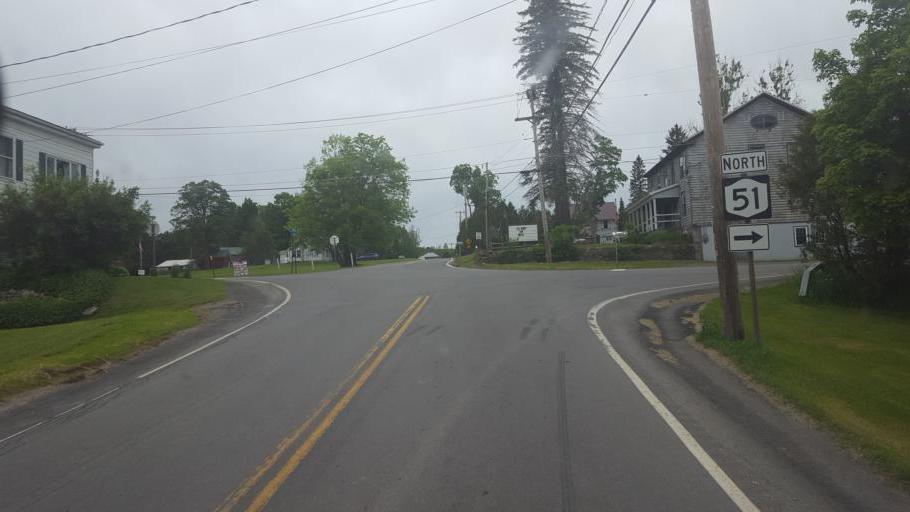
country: US
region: New York
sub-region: Herkimer County
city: Ilion
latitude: 42.9313
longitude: -75.1150
